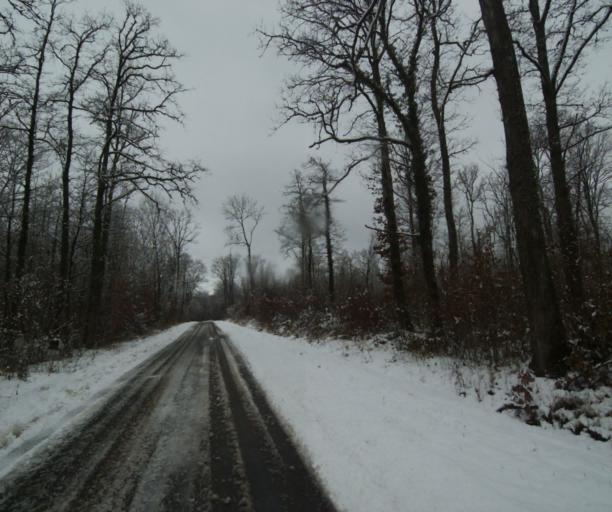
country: FR
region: Champagne-Ardenne
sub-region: Departement de la Haute-Marne
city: Wassy
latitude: 48.4587
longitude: 4.9383
